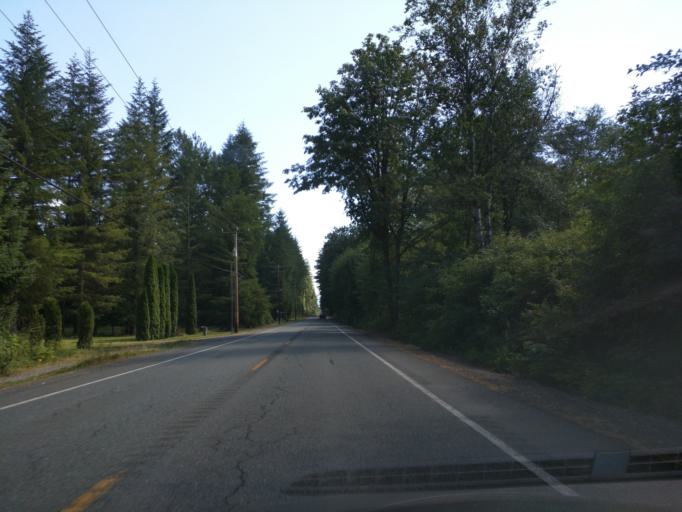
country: US
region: Washington
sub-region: Whatcom County
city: Peaceful Valley
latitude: 48.9326
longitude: -122.1435
